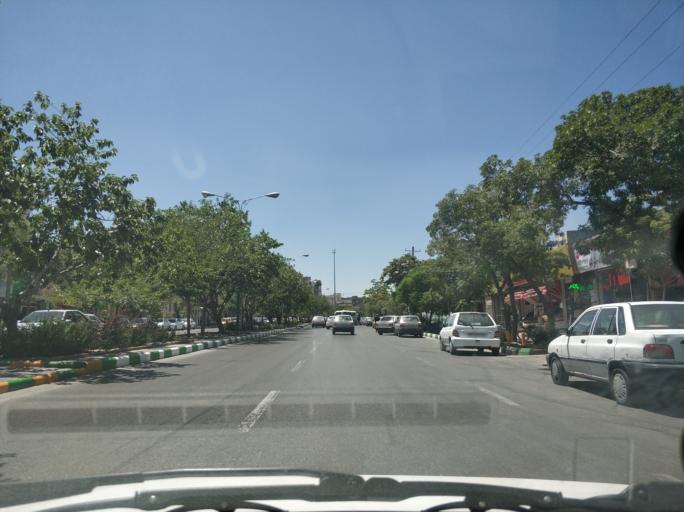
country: IR
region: Razavi Khorasan
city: Mashhad
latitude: 36.3148
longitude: 59.4864
